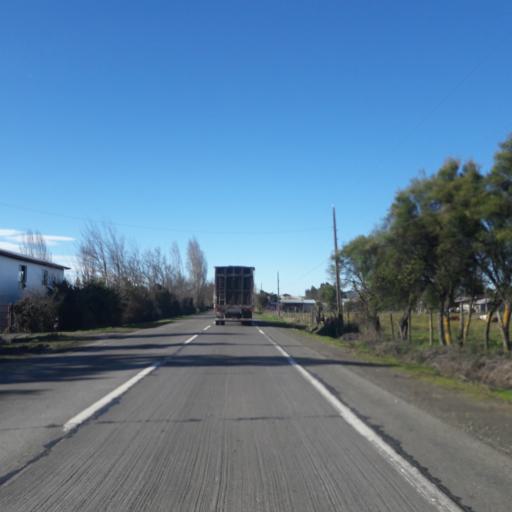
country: CL
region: Araucania
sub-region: Provincia de Malleco
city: Angol
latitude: -37.7781
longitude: -72.5387
